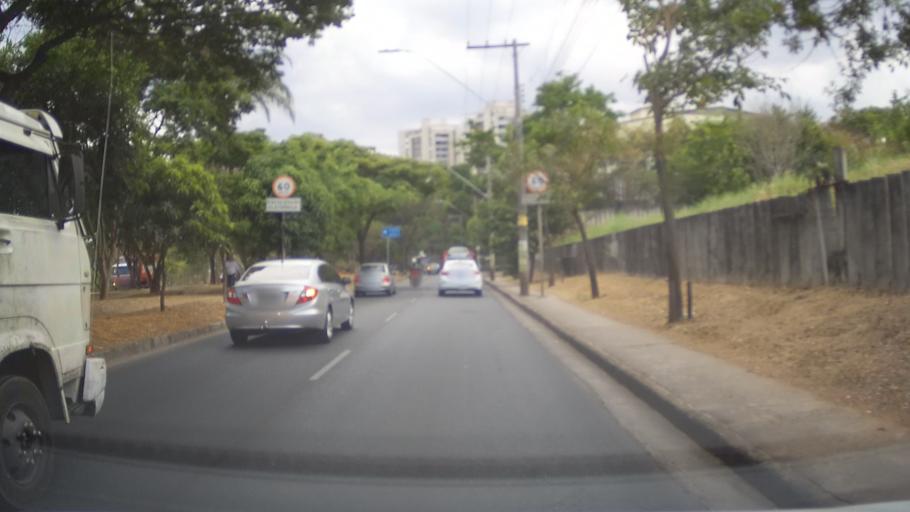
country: BR
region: Minas Gerais
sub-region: Belo Horizonte
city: Belo Horizonte
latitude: -19.8845
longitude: -43.9168
